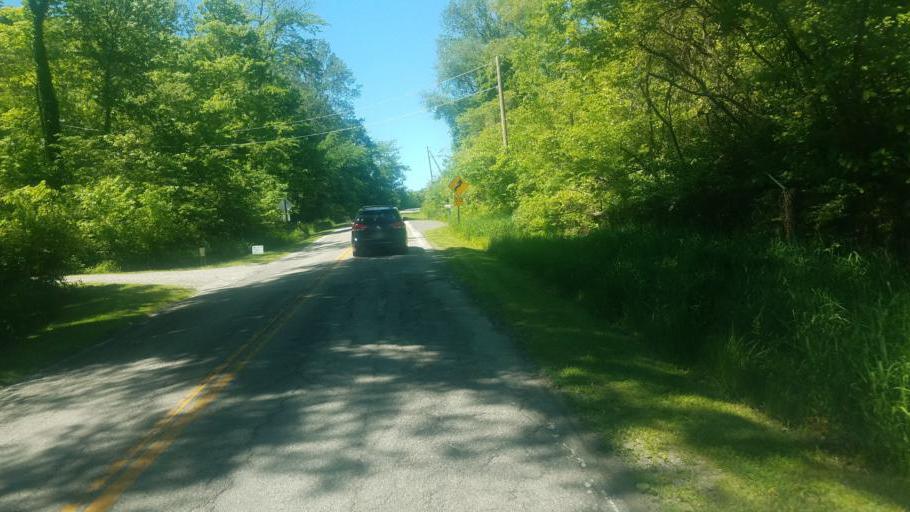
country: US
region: Ohio
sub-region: Champaign County
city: Saint Paris
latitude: 40.1881
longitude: -83.9550
